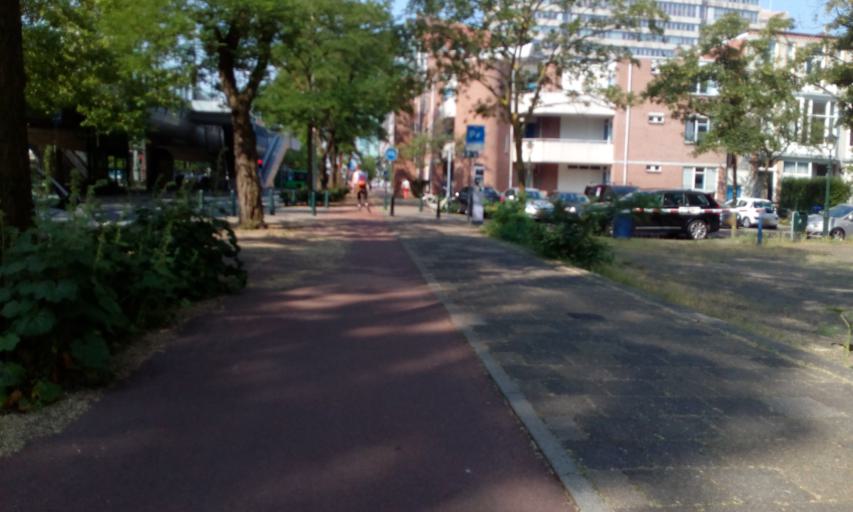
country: NL
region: South Holland
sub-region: Gemeente Leidschendam-Voorburg
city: Voorburg
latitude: 52.0827
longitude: 4.3339
